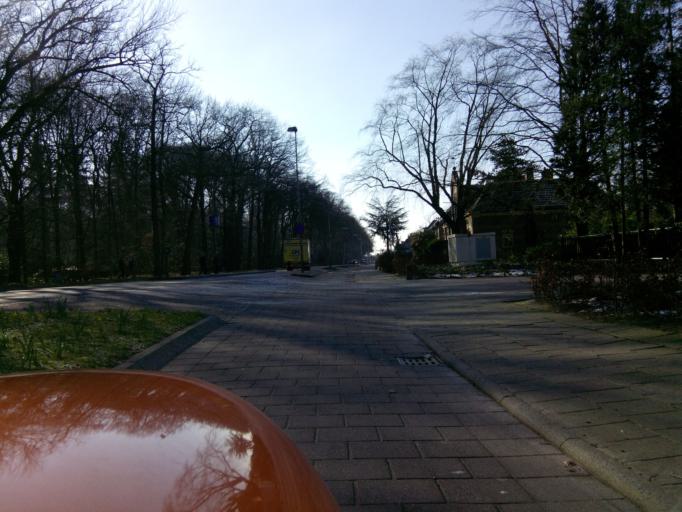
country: NL
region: Gelderland
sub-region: Gemeente Barneveld
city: Barneveld
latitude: 52.1502
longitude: 5.5944
